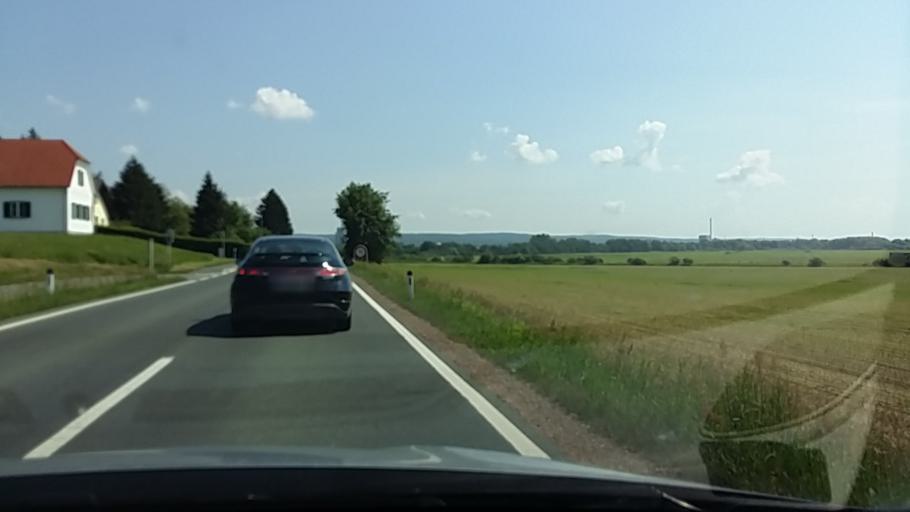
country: AT
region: Burgenland
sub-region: Politischer Bezirk Jennersdorf
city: Mogersdorf
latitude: 46.9592
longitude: 16.2466
